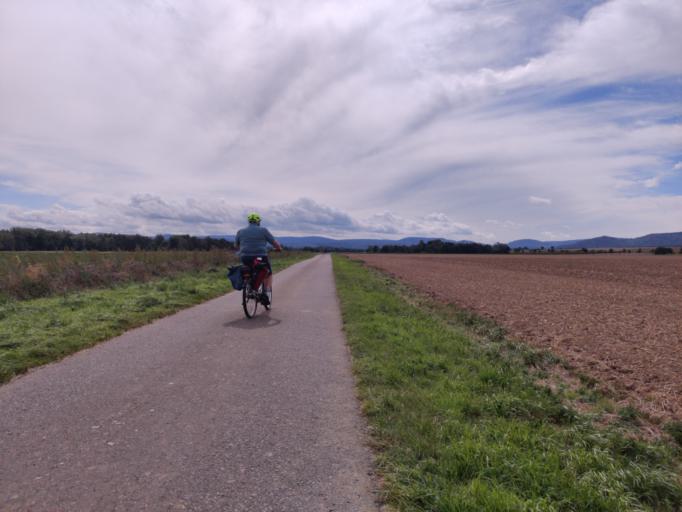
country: DE
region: Lower Saxony
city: Liebenburg
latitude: 51.9956
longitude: 10.3707
